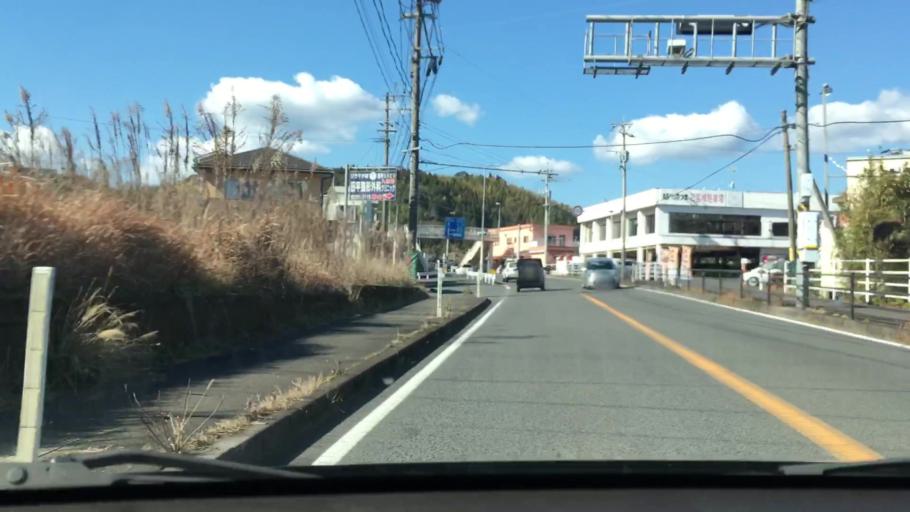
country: JP
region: Kagoshima
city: Ijuin
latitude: 31.6621
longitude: 130.4897
